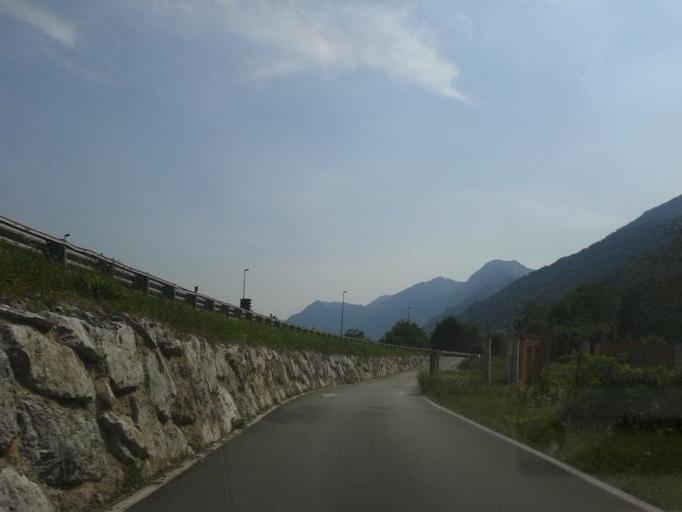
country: IT
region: Trentino-Alto Adige
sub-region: Provincia di Trento
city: Storo
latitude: 45.8513
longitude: 10.5638
